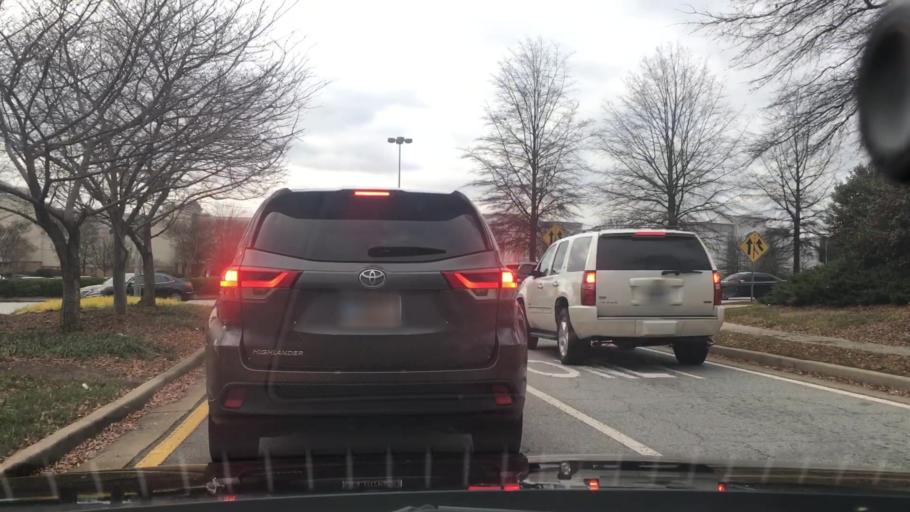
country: US
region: Georgia
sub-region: DeKalb County
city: Lithonia
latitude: 33.6983
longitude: -84.0918
